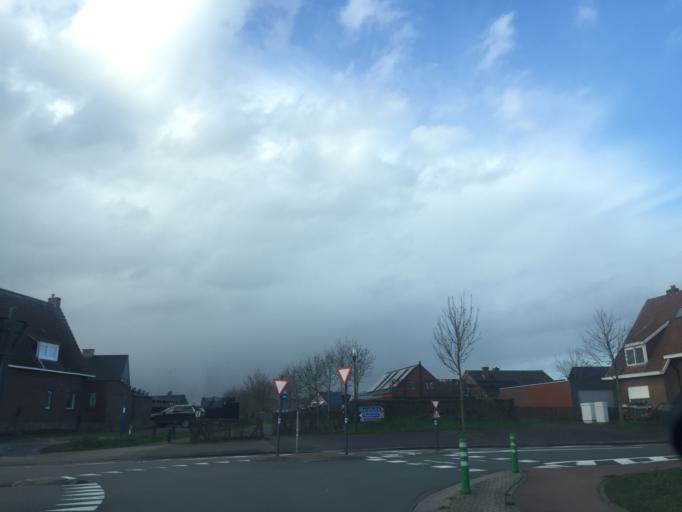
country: BE
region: Flanders
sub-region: Provincie West-Vlaanderen
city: Harelbeke
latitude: 50.8333
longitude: 3.3236
